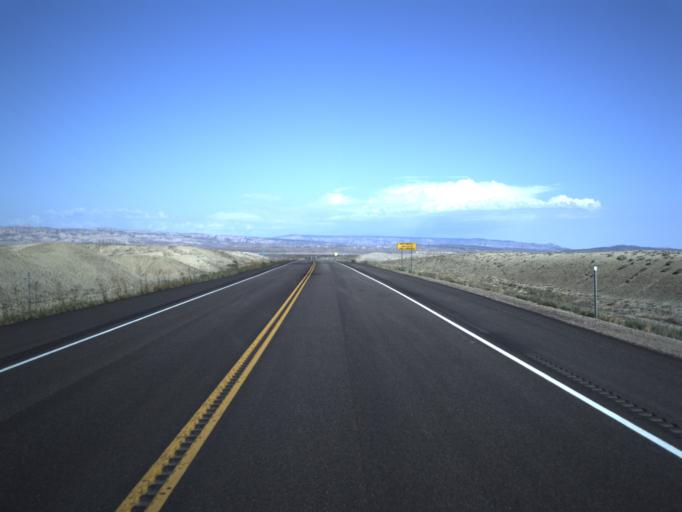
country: US
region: Utah
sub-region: Carbon County
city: East Carbon City
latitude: 38.9889
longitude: -110.2454
